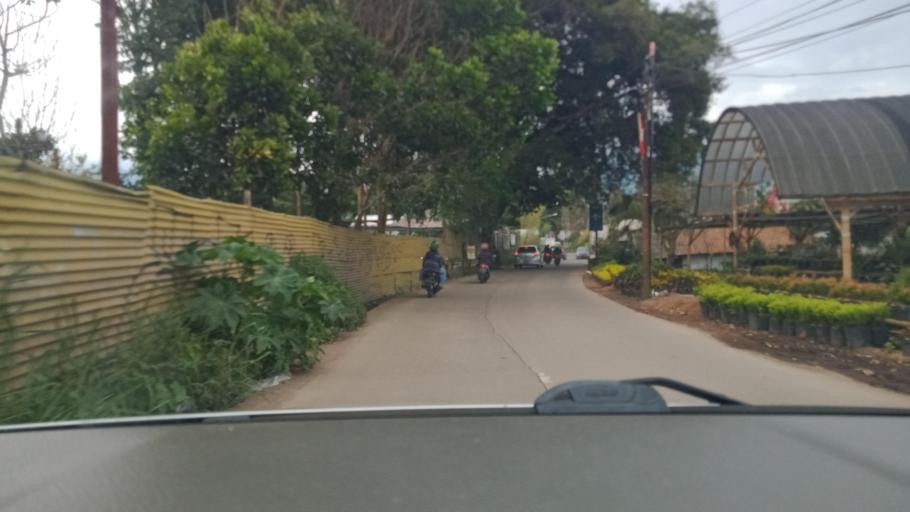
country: ID
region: West Java
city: Lembang
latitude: -6.8201
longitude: 107.5949
